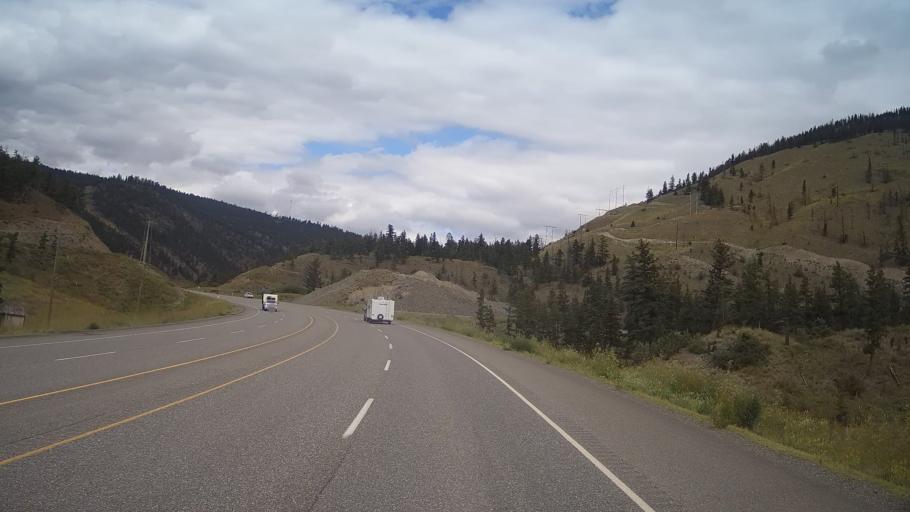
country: CA
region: British Columbia
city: Cache Creek
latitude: 50.9854
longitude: -121.5141
